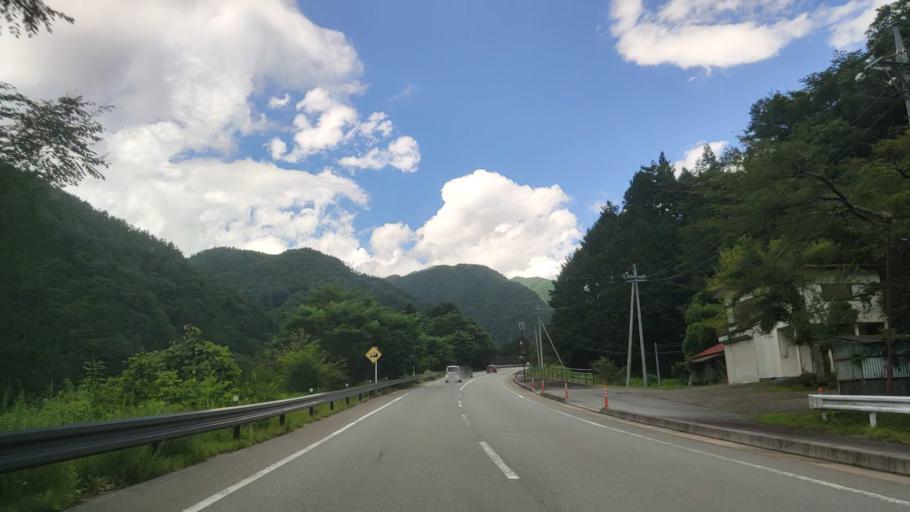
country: JP
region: Yamanashi
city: Enzan
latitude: 35.8093
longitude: 138.7514
